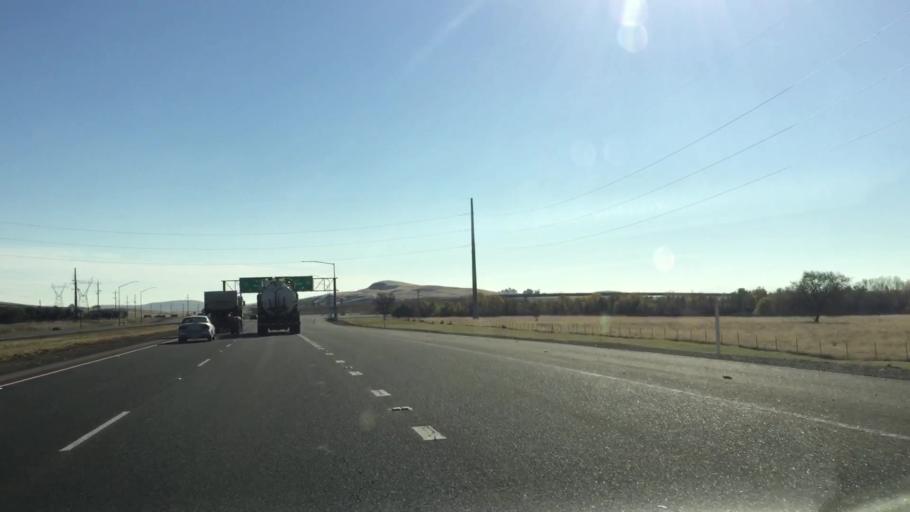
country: US
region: California
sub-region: Butte County
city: Thermalito
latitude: 39.5906
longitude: -121.6205
